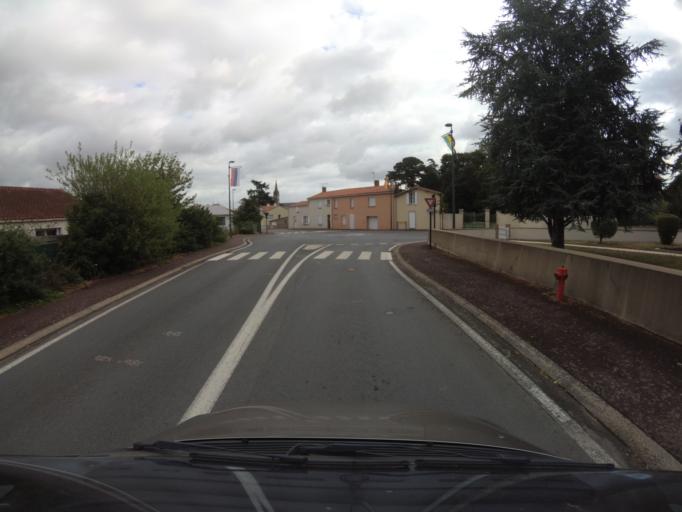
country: FR
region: Pays de la Loire
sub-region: Departement de la Vendee
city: Cugand
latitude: 47.0608
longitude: -1.2564
